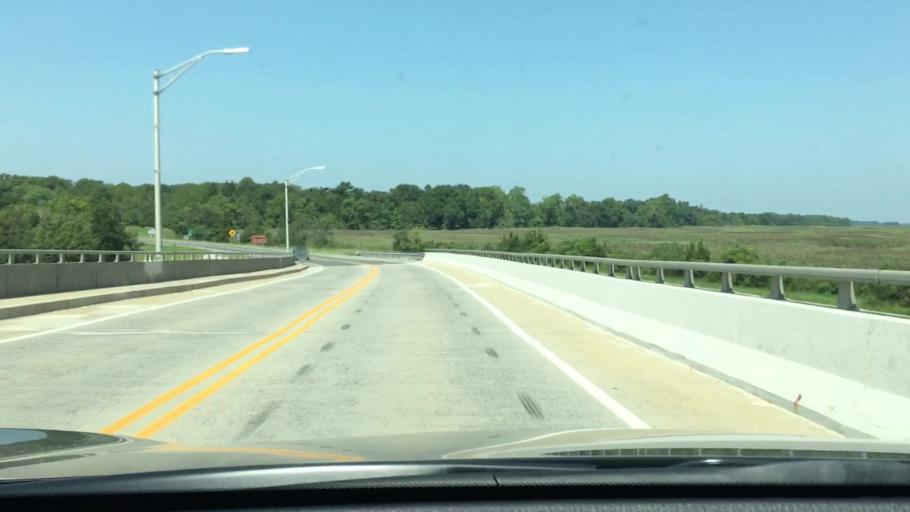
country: US
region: New Jersey
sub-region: Cumberland County
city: Port Norris
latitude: 39.2886
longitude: -74.9905
